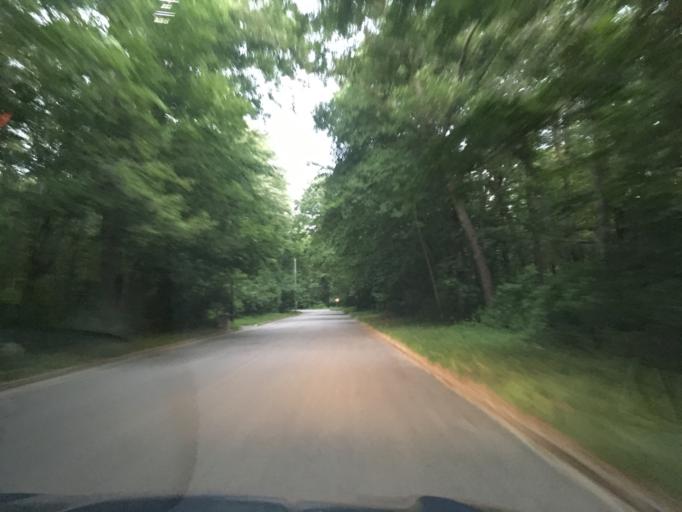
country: US
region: Rhode Island
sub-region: Washington County
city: Exeter
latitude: 41.6309
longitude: -71.5161
